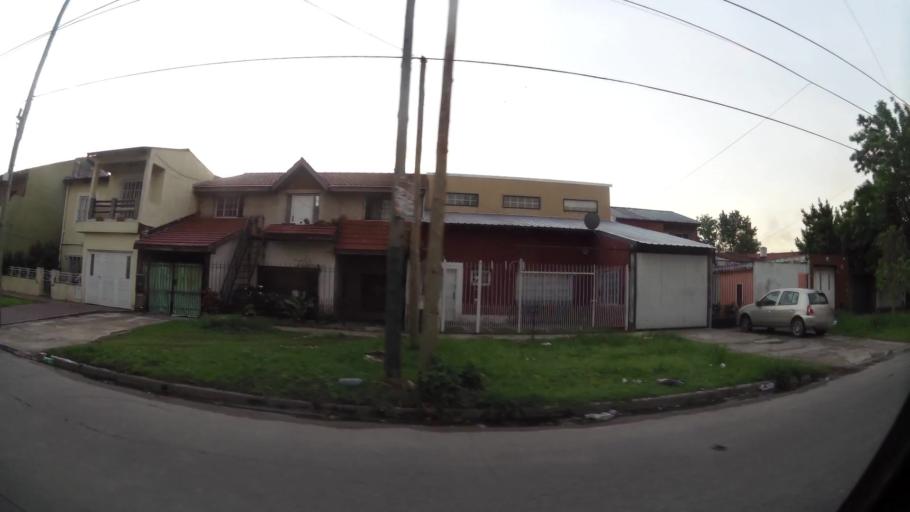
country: AR
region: Buenos Aires
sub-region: Partido de Lomas de Zamora
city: Lomas de Zamora
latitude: -34.7576
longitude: -58.3686
